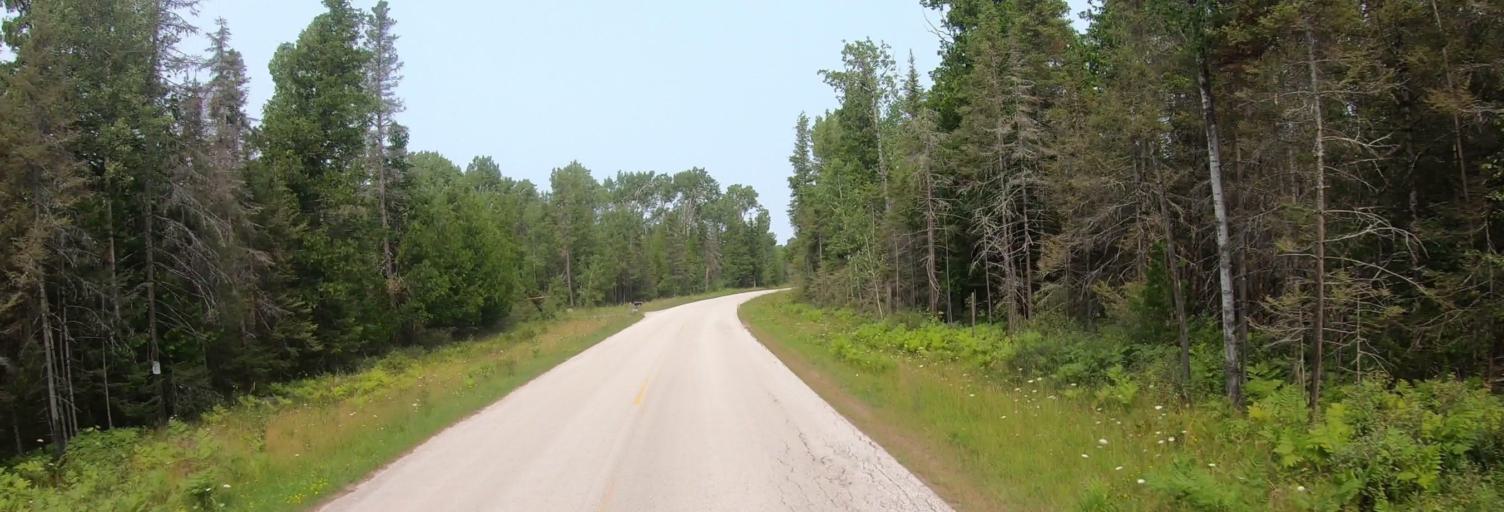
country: CA
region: Ontario
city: Thessalon
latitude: 46.0628
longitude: -83.6652
